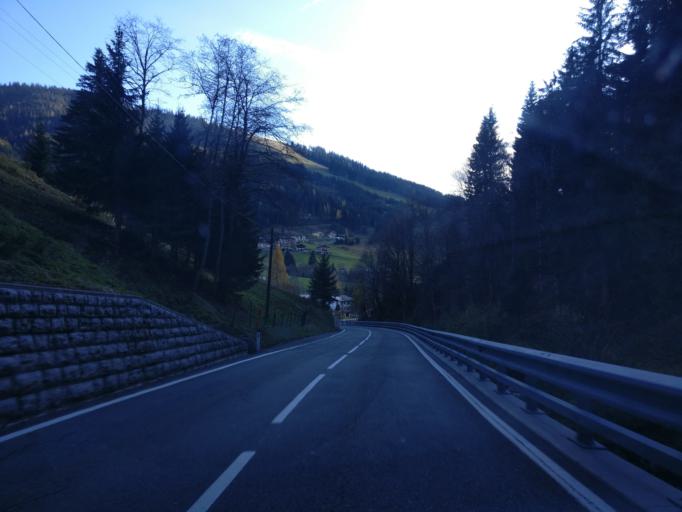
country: AT
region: Salzburg
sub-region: Politischer Bezirk Zell am See
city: Dienten am Hochkonig
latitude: 47.3916
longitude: 13.0156
